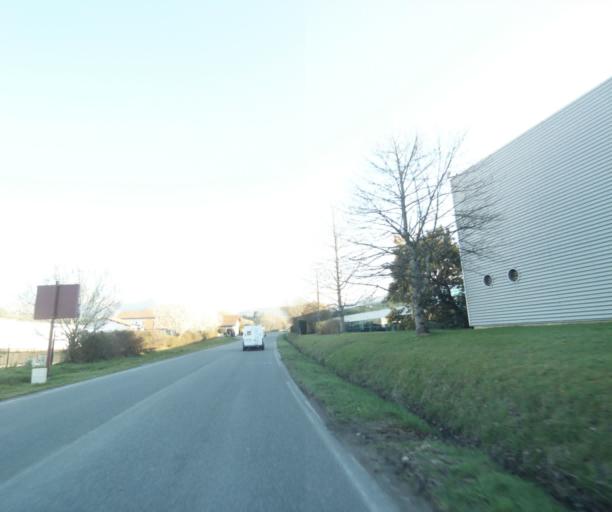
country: FR
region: Aquitaine
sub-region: Departement des Pyrenees-Atlantiques
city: Urrugne
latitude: 43.3521
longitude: -1.6893
